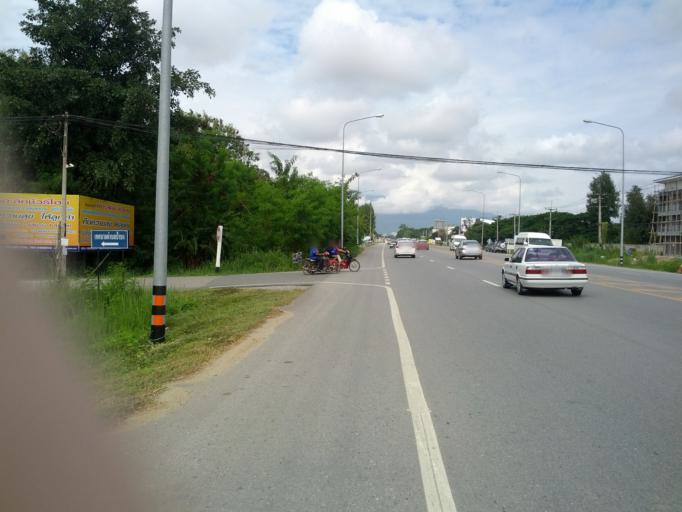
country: TH
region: Chiang Mai
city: Saraphi
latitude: 18.7550
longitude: 99.0542
